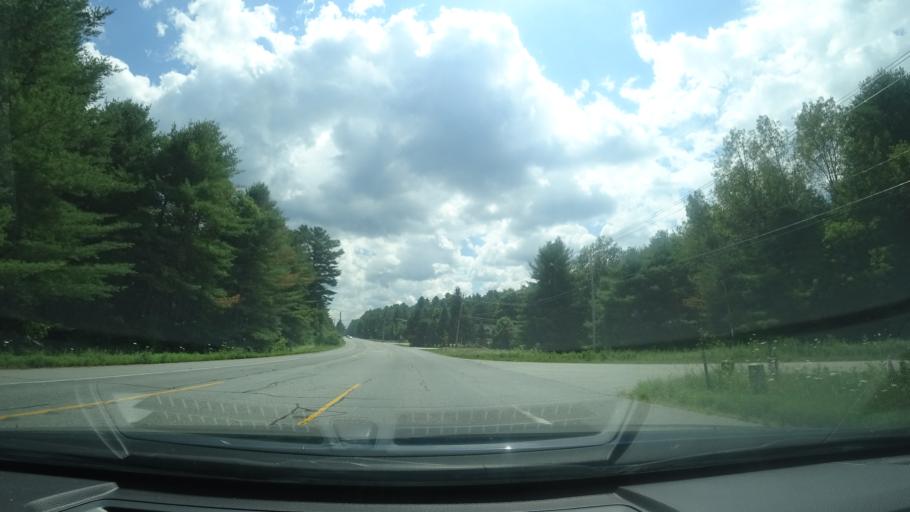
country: US
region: New York
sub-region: Warren County
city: Warrensburg
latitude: 43.5350
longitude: -73.7967
